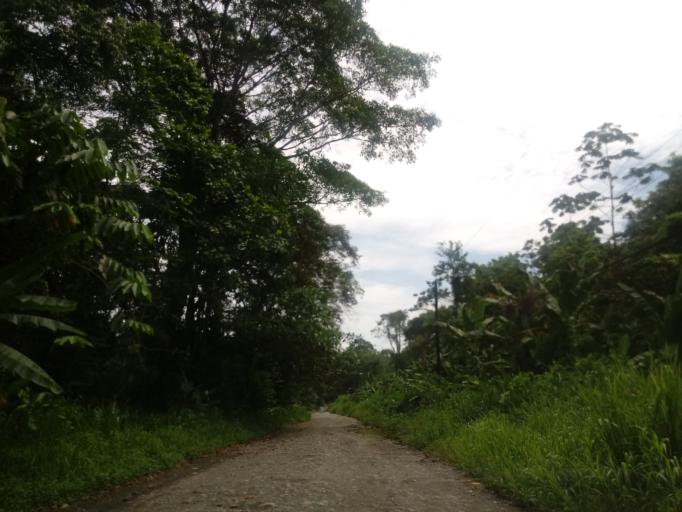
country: CR
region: Limon
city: Limon
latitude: 9.7524
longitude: -82.8814
